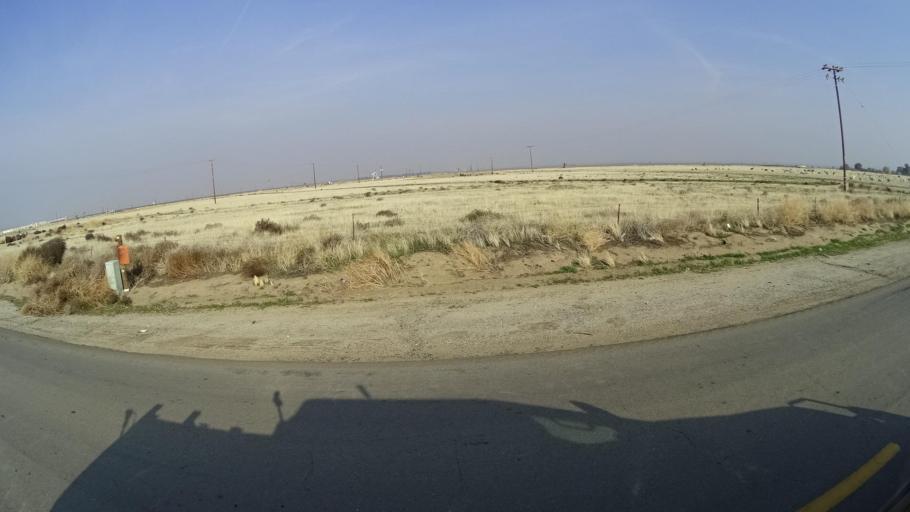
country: US
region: California
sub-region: Kern County
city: Lebec
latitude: 34.9844
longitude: -118.9183
